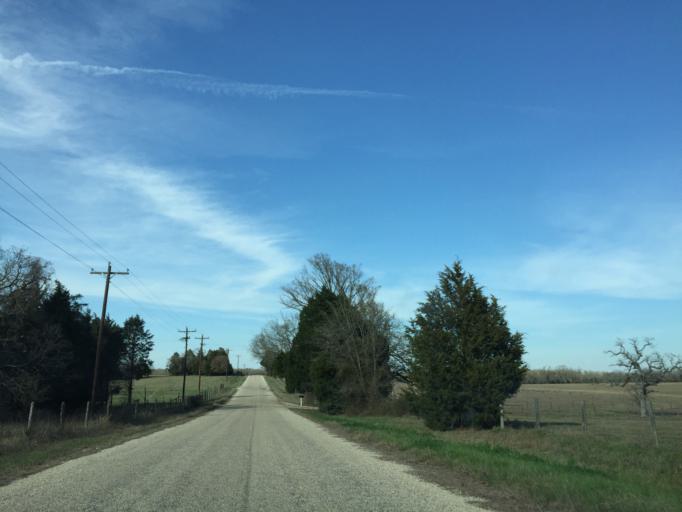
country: US
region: Texas
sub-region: Milam County
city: Thorndale
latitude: 30.4542
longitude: -97.1926
